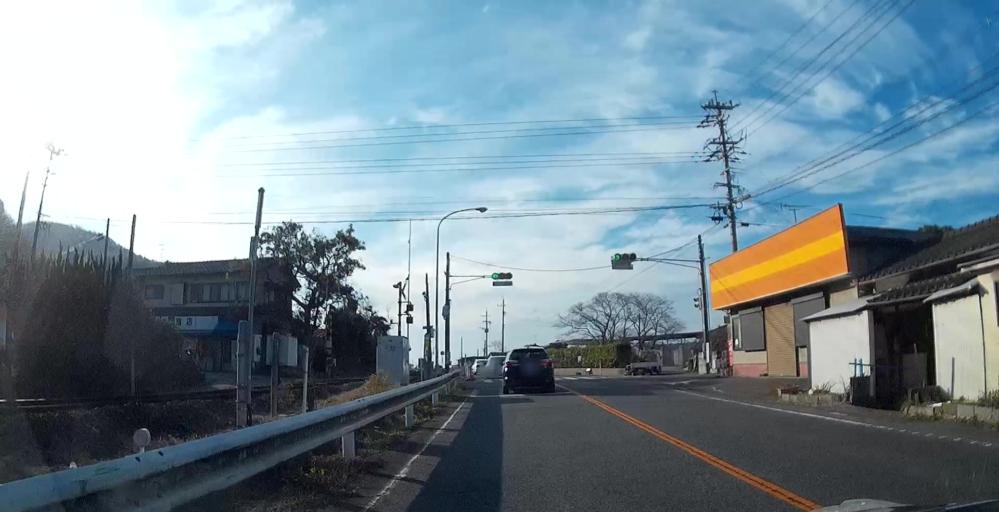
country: JP
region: Kumamoto
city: Uto
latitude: 32.7043
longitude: 130.5902
